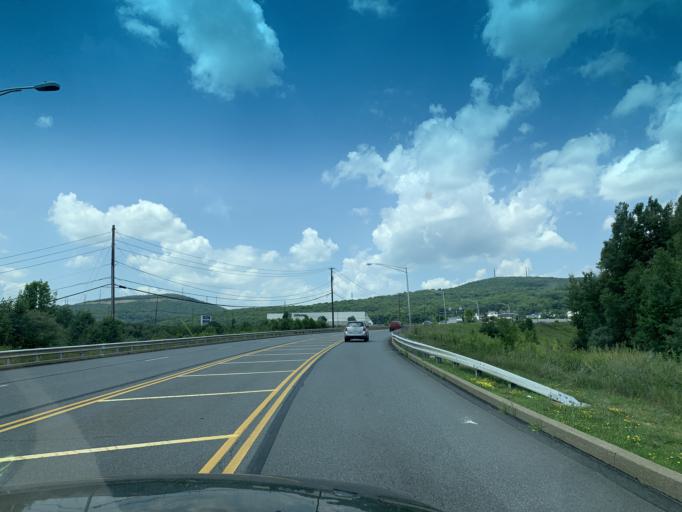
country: US
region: Pennsylvania
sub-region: Lackawanna County
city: Chinchilla
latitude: 41.4565
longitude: -75.6502
